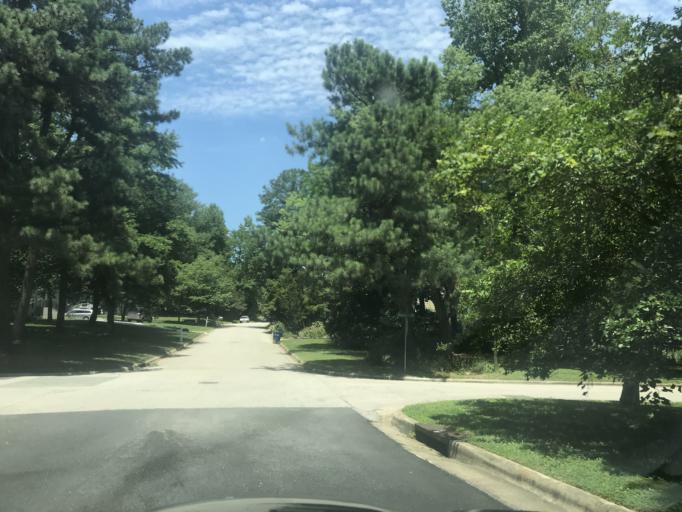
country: US
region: North Carolina
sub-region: Wake County
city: West Raleigh
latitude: 35.8918
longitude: -78.6234
